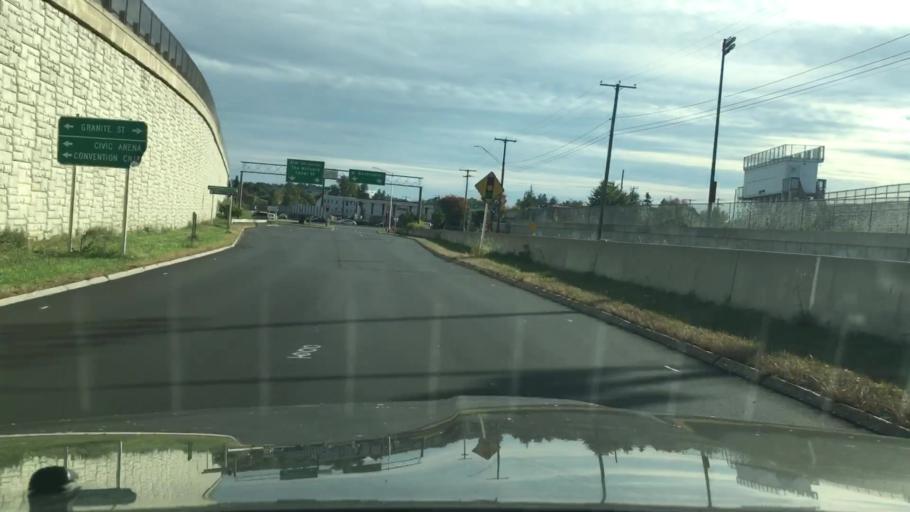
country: US
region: New Hampshire
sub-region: Hillsborough County
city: Manchester
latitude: 42.9865
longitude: -71.4721
